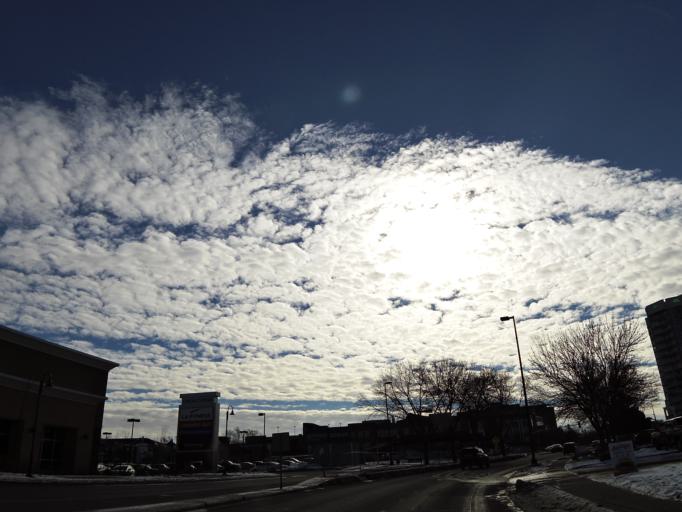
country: US
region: Minnesota
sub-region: Hennepin County
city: Richfield
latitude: 44.8848
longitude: -93.2860
